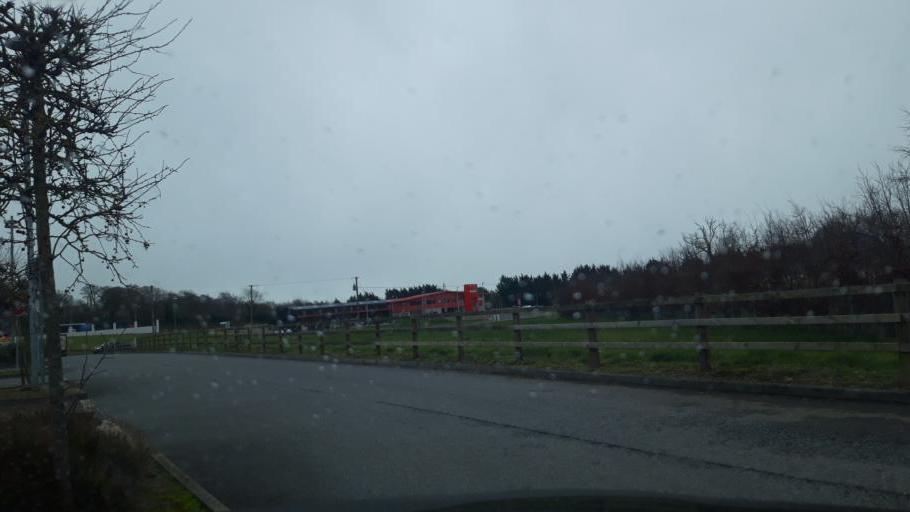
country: IE
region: Leinster
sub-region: Kilkenny
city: Kilkenny
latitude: 52.6507
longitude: -7.2127
